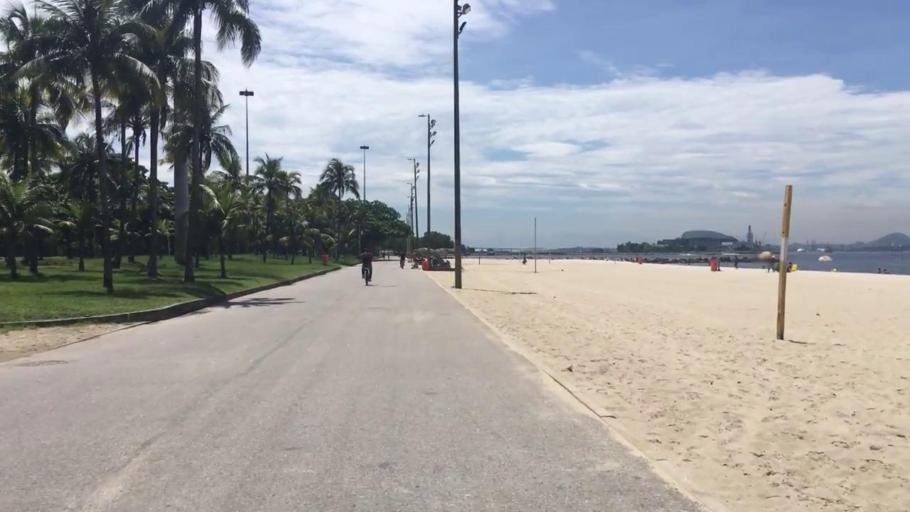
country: BR
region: Rio de Janeiro
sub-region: Rio De Janeiro
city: Rio de Janeiro
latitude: -22.9242
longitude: -43.1695
